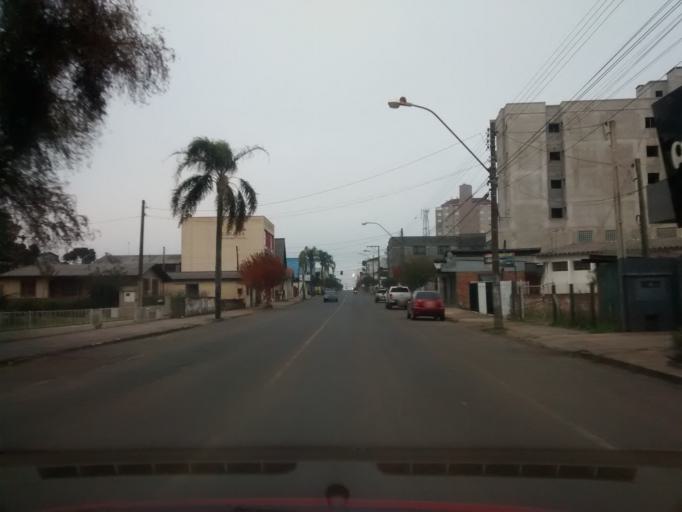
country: BR
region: Rio Grande do Sul
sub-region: Vacaria
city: Vacaria
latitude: -28.5047
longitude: -50.9323
